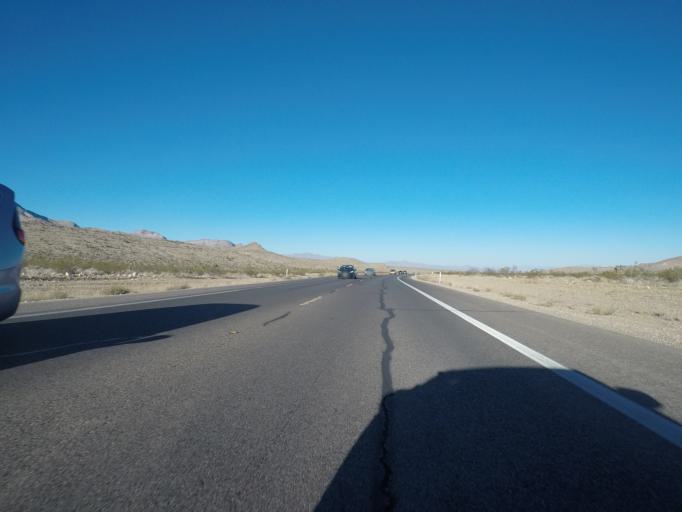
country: US
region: Nevada
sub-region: Clark County
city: Summerlin South
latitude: 36.1371
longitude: -115.4077
